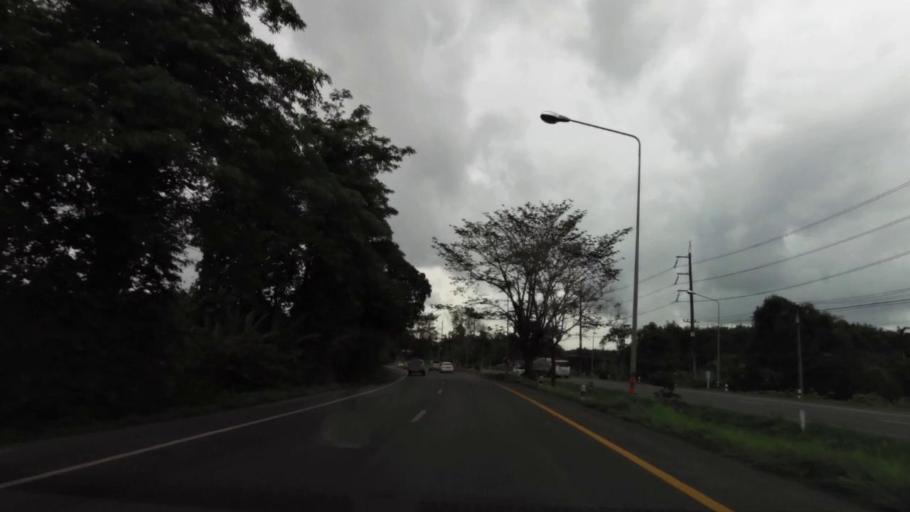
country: TH
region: Chanthaburi
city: Tha Mai
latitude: 12.6824
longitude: 102.0050
